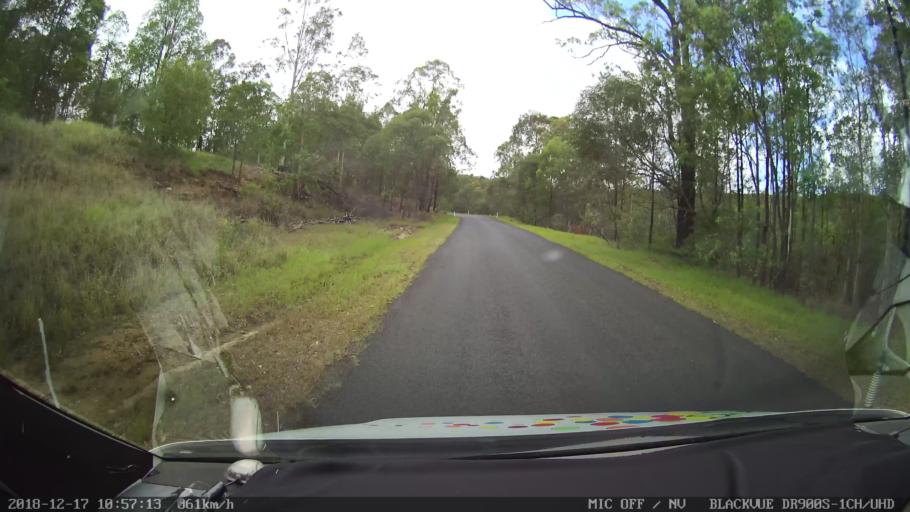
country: AU
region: New South Wales
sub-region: Richmond Valley
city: Casino
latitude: -28.8244
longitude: 152.5948
